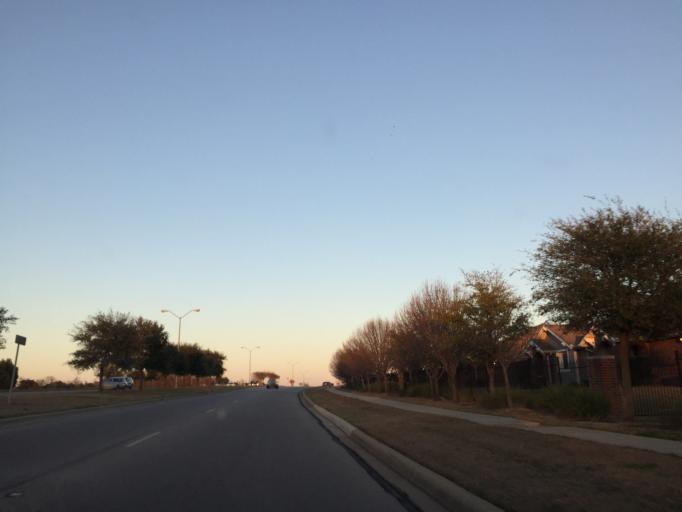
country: US
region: Texas
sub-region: Travis County
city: Pflugerville
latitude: 30.4311
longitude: -97.6216
